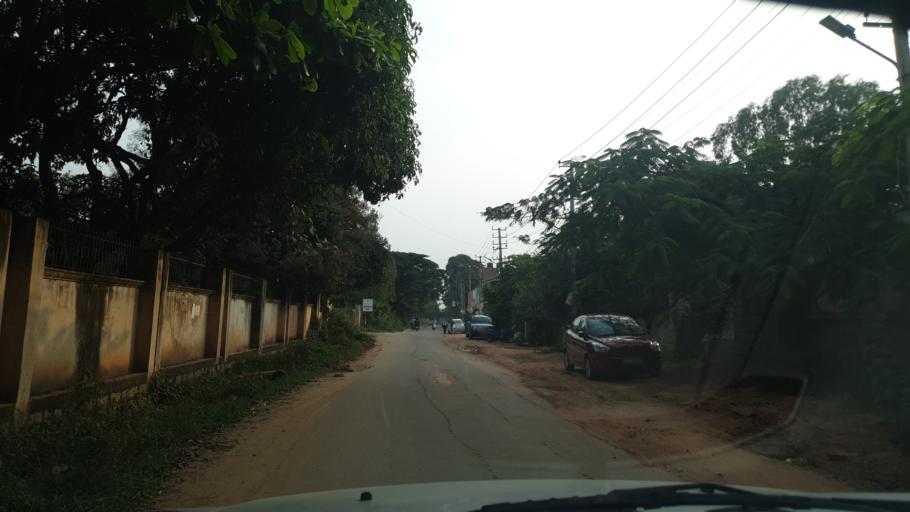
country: IN
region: Karnataka
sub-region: Bangalore Urban
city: Yelahanka
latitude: 13.0638
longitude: 77.6556
